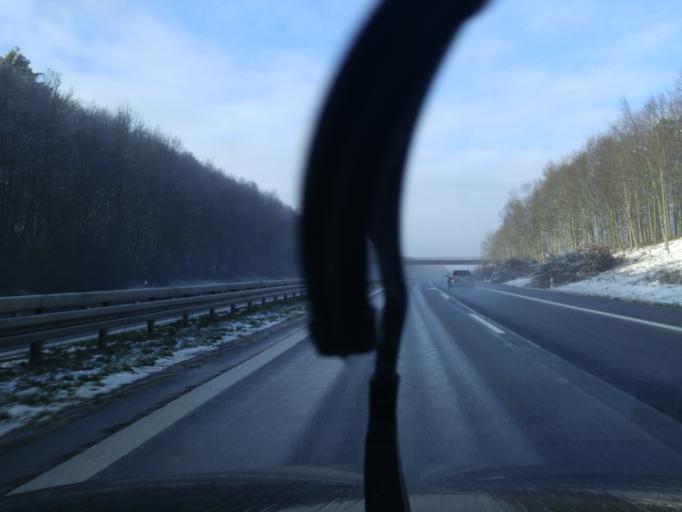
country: DE
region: Bavaria
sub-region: Regierungsbezirk Unterfranken
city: Wasserlosen
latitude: 50.0747
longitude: 10.0183
